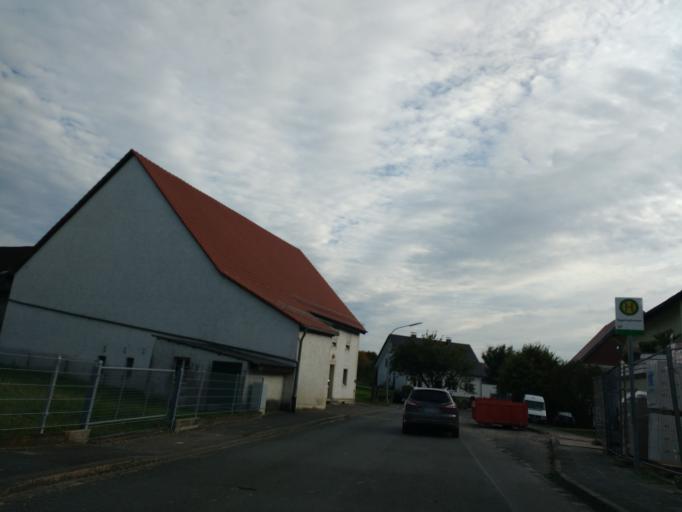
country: DE
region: North Rhine-Westphalia
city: Lichtenau
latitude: 51.6637
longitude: 8.8356
